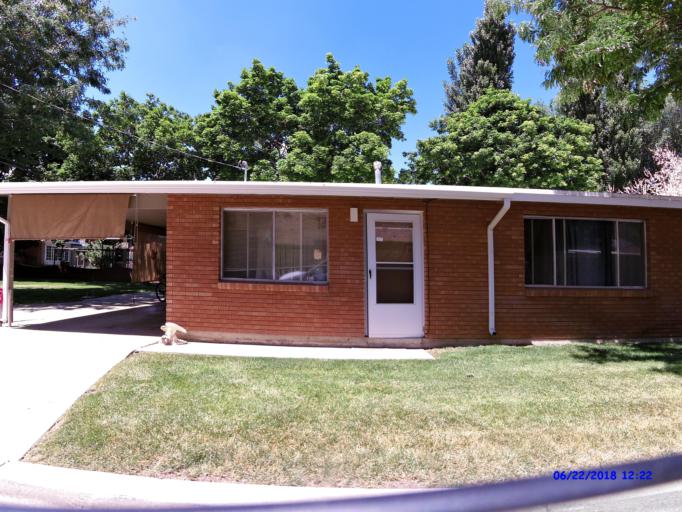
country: US
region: Utah
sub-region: Weber County
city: Ogden
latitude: 41.2419
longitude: -111.9651
